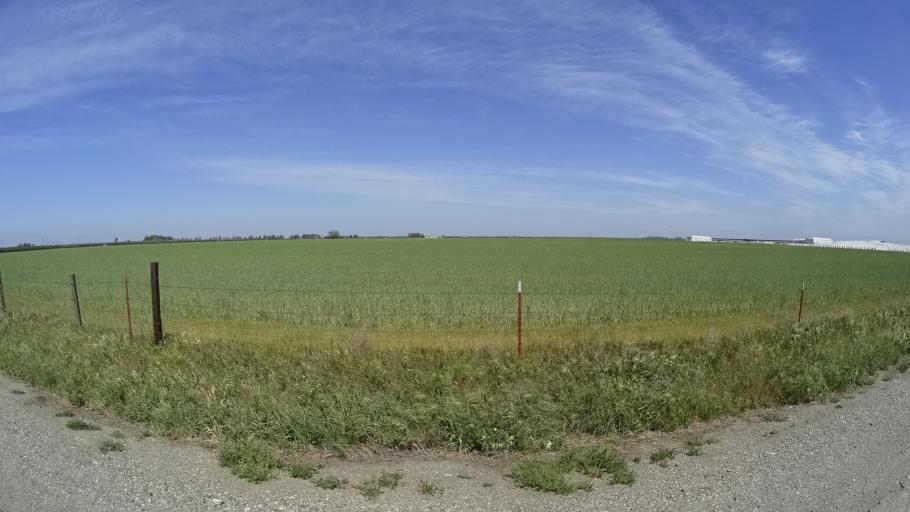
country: US
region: California
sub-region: Glenn County
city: Orland
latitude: 39.6531
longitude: -122.1740
